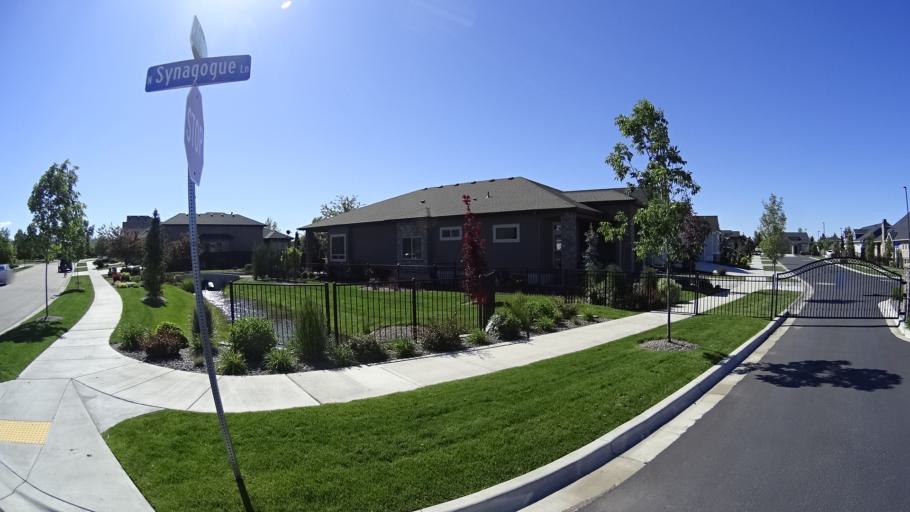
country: US
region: Idaho
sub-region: Ada County
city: Meridian
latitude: 43.6679
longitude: -116.4092
